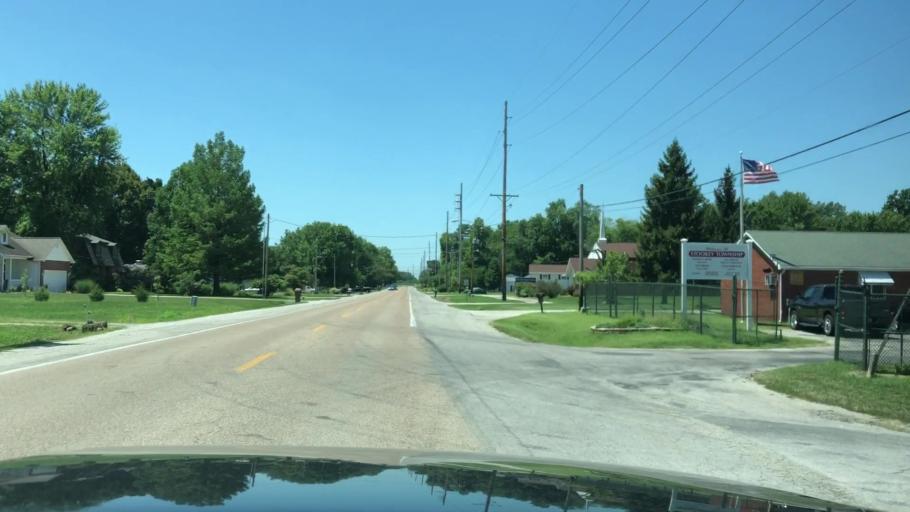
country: US
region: Illinois
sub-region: Saint Clair County
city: Centreville
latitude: 38.5451
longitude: -90.0746
